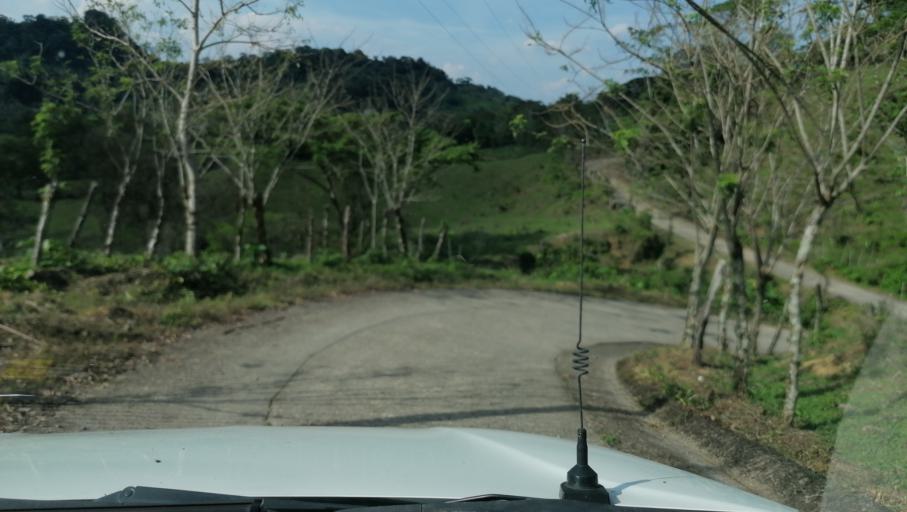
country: MX
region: Chiapas
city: Ostuacan
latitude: 17.4676
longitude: -93.2366
